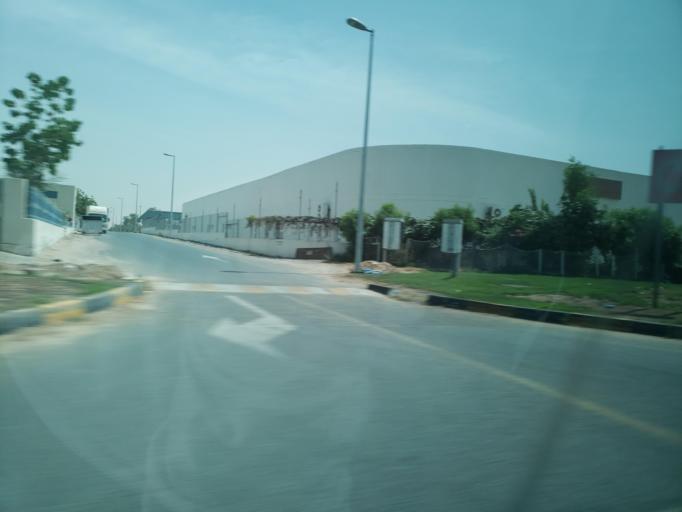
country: AE
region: Ash Shariqah
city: Sharjah
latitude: 25.3309
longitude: 55.4941
